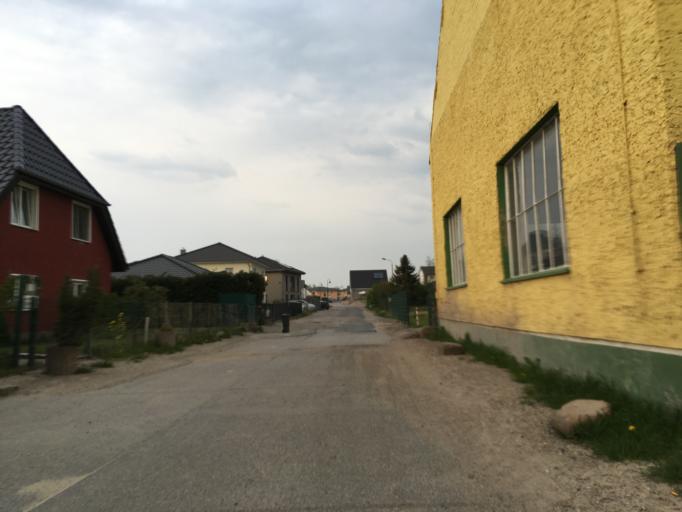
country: DE
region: Berlin
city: Wartenberg
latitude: 52.6006
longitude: 13.5231
